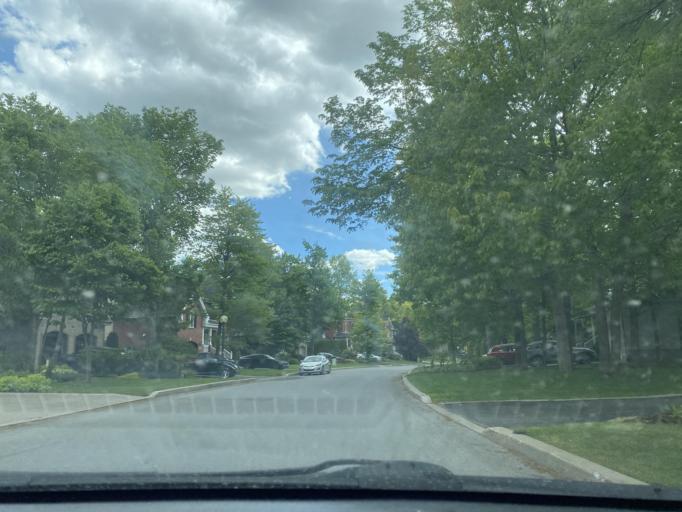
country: CA
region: Quebec
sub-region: Monteregie
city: Chambly
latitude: 45.4695
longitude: -73.2906
